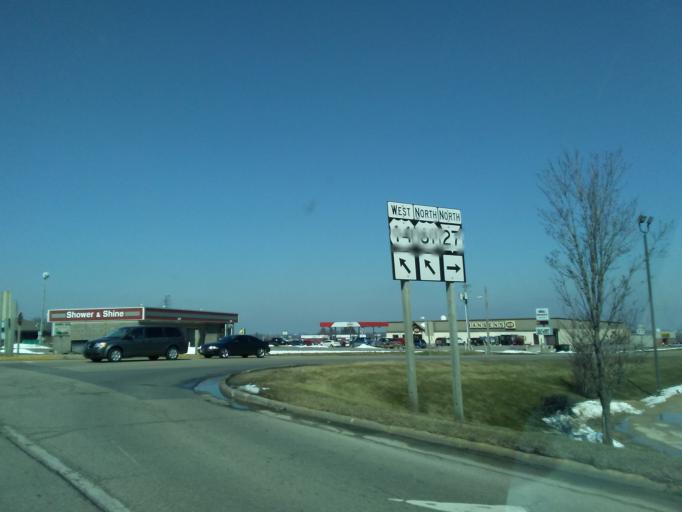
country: US
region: Wisconsin
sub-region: Vernon County
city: Westby
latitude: 43.6589
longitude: -90.8565
